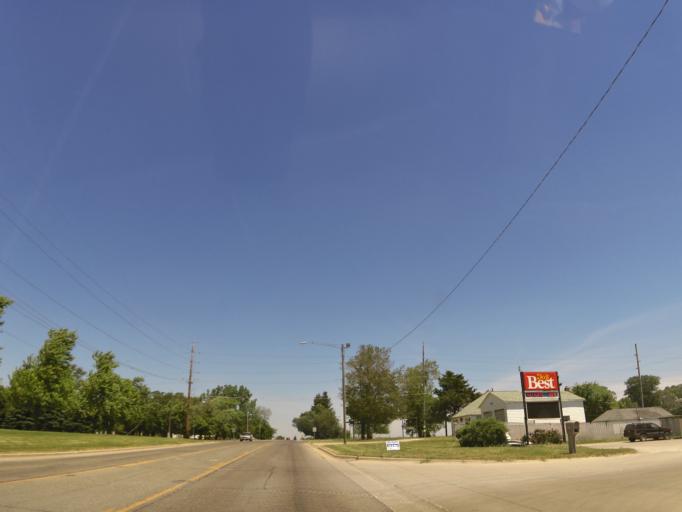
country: US
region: Illinois
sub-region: Vermilion County
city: Hoopeston
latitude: 40.4725
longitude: -87.6878
